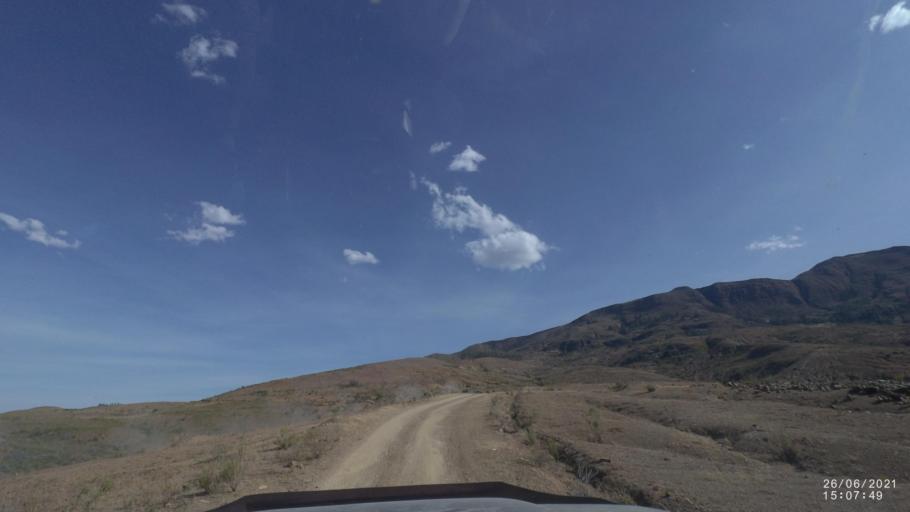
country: BO
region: Cochabamba
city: Mizque
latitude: -17.9447
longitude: -65.6390
